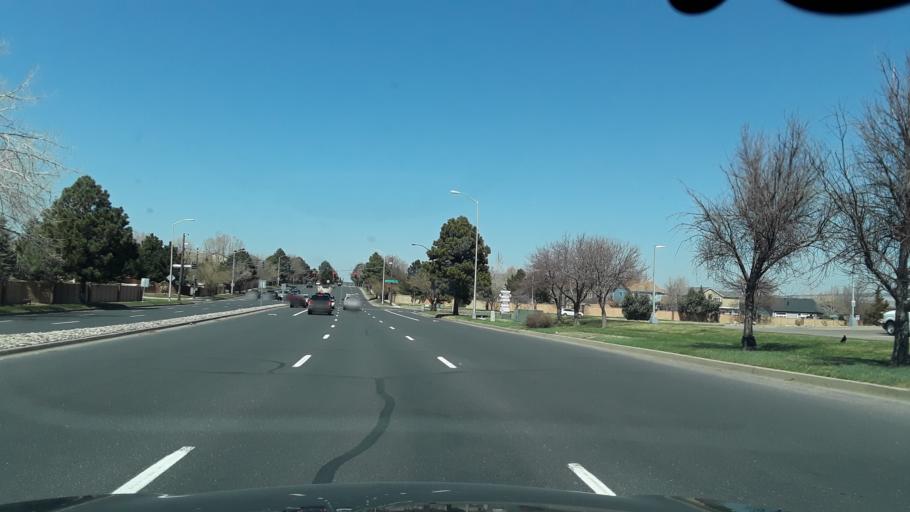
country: US
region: Colorado
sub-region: El Paso County
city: Cimarron Hills
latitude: 38.9151
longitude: -104.7338
